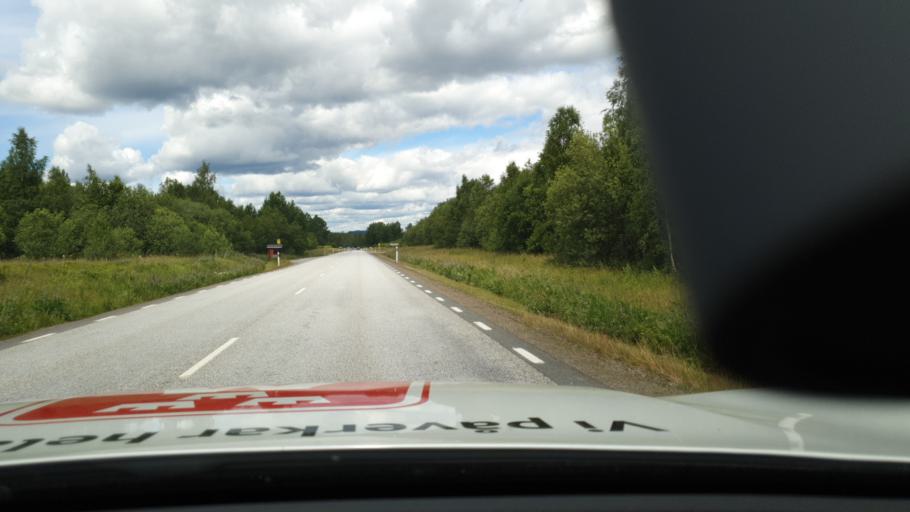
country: SE
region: Vaermland
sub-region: Storfors Kommun
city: Storfors
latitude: 59.5284
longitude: 14.2969
